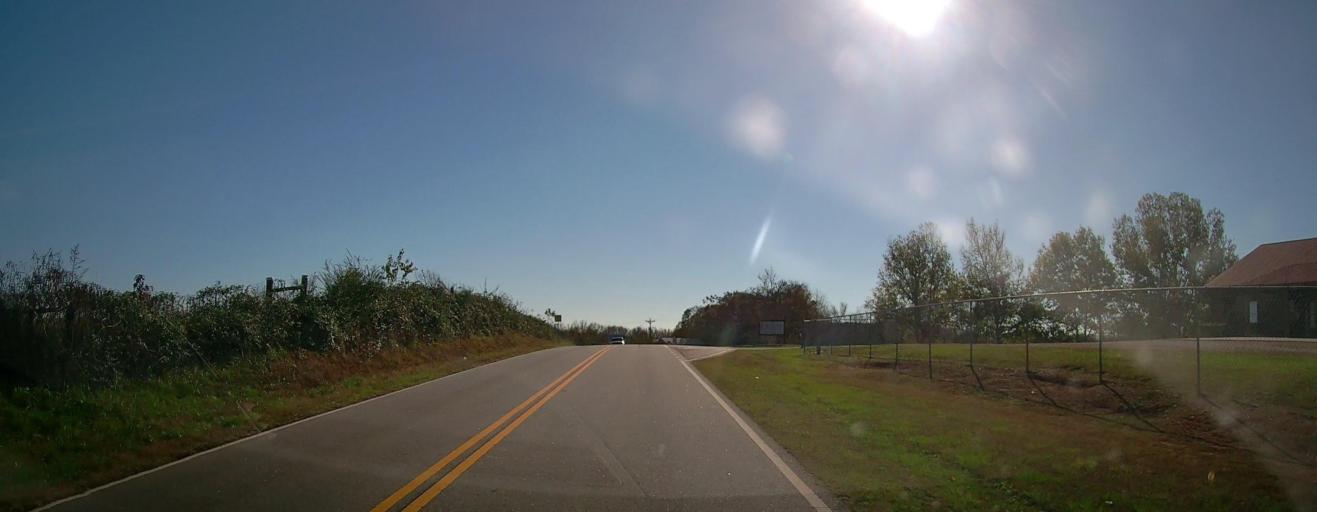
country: US
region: Georgia
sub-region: Hall County
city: Lula
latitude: 34.4668
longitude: -83.7348
